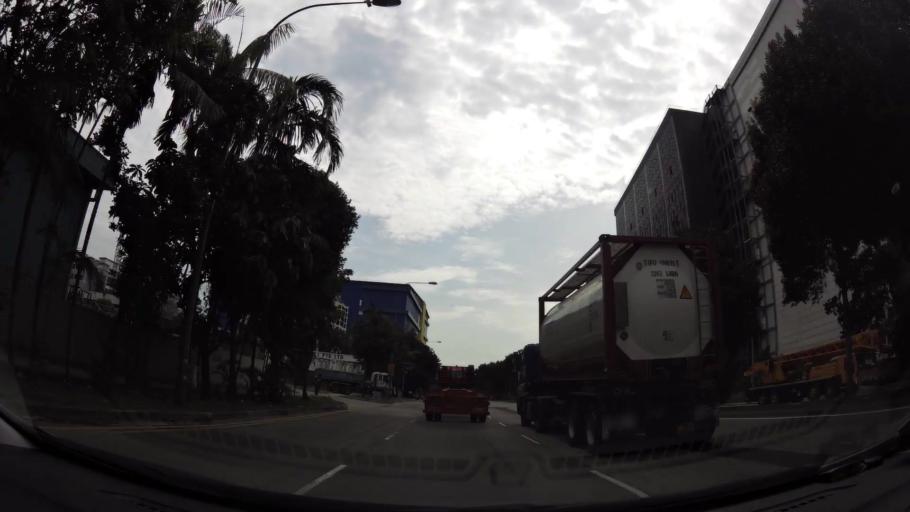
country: SG
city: Singapore
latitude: 1.3141
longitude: 103.7211
